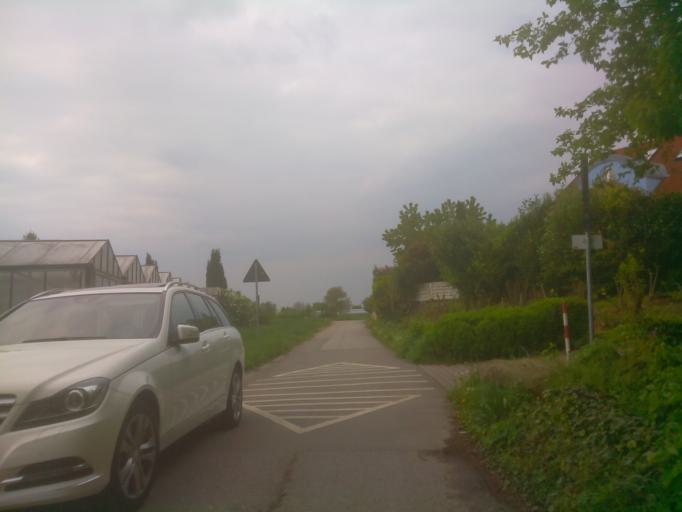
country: DE
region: Baden-Wuerttemberg
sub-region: Karlsruhe Region
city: Dossenheim
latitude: 49.4449
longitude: 8.6650
